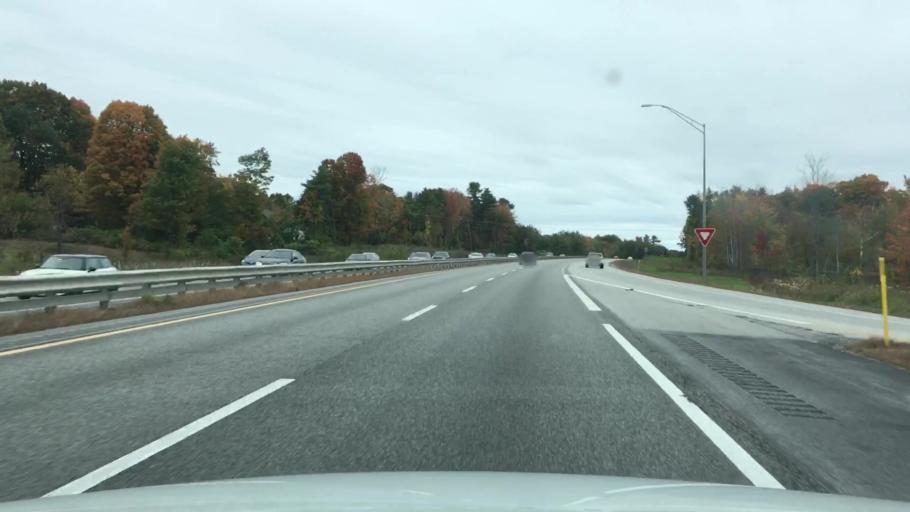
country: US
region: Maine
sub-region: Cumberland County
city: Freeport
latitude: 43.8660
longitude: -70.1064
